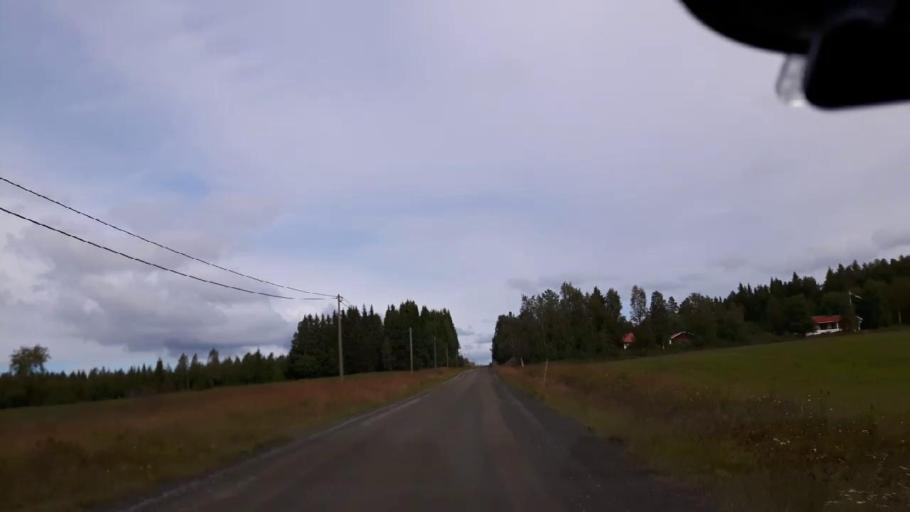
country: SE
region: Jaemtland
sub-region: Krokoms Kommun
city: Krokom
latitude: 63.3610
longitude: 14.1292
